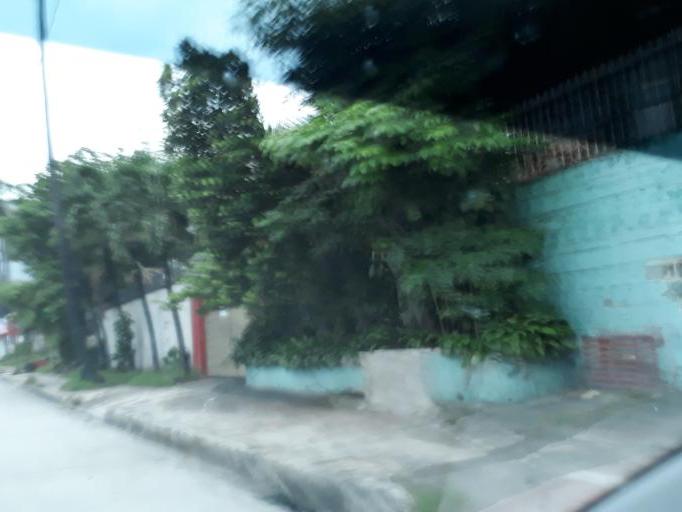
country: PH
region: Calabarzon
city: Del Monte
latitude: 14.6421
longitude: 121.0004
